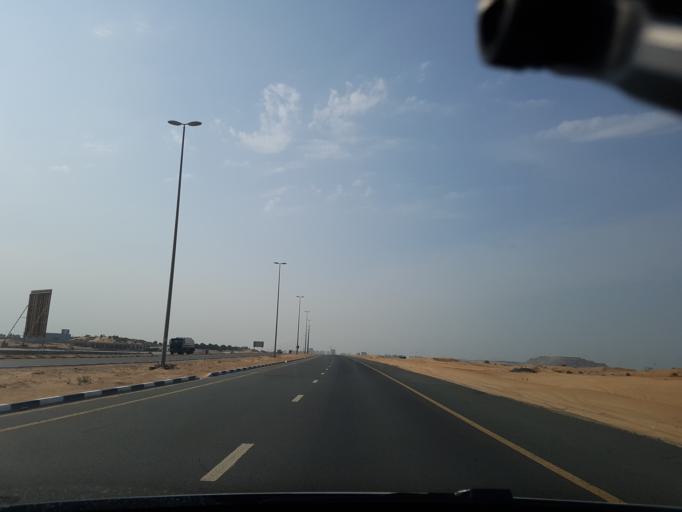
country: AE
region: Ajman
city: Ajman
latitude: 25.4091
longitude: 55.5710
